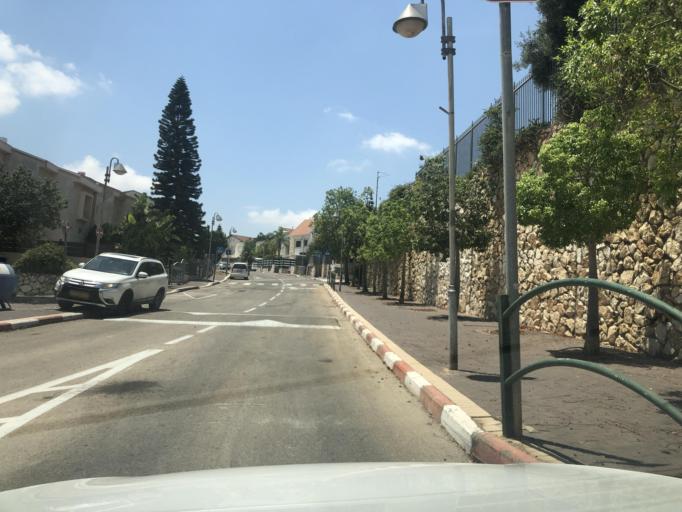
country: IL
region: Haifa
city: Daliyat el Karmil
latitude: 32.6386
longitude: 35.0910
